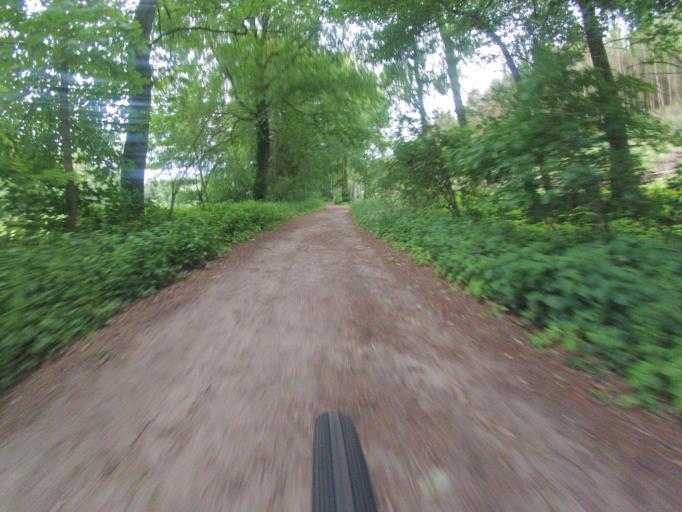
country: DE
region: North Rhine-Westphalia
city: Ibbenburen
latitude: 52.2363
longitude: 7.7400
